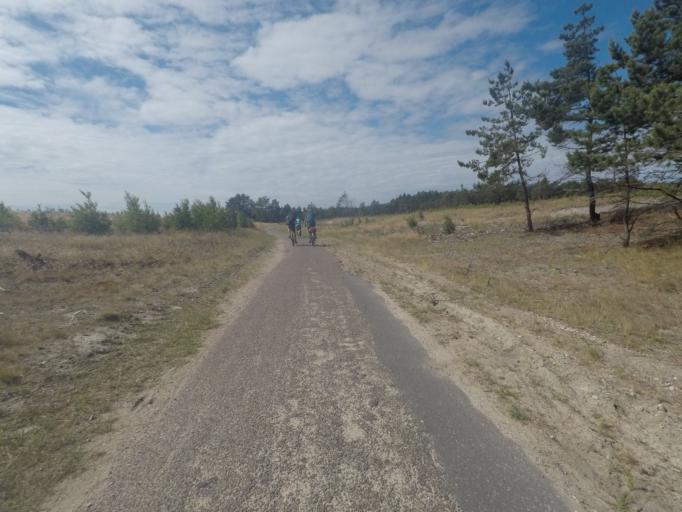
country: LT
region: Klaipedos apskritis
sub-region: Klaipeda
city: Klaipeda
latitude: 55.5922
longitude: 21.1145
